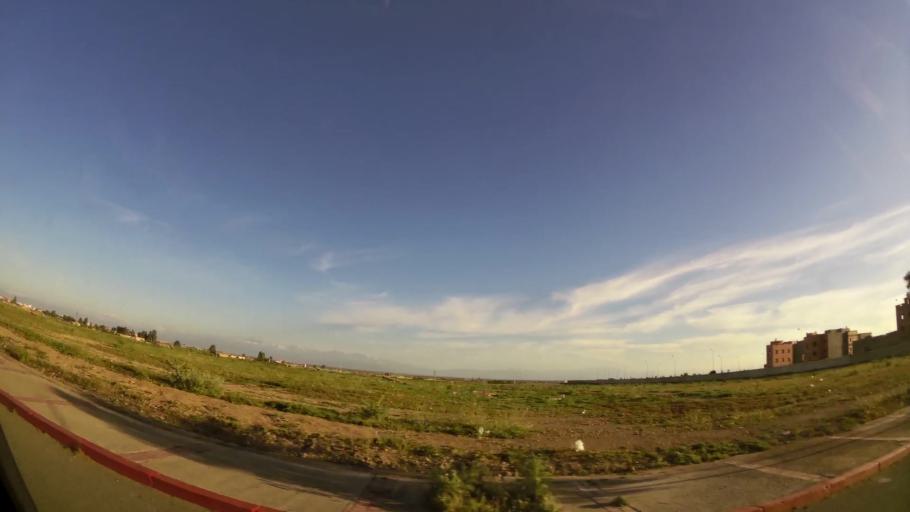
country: MA
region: Marrakech-Tensift-Al Haouz
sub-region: Marrakech
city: Marrakesh
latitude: 31.7428
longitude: -8.1185
